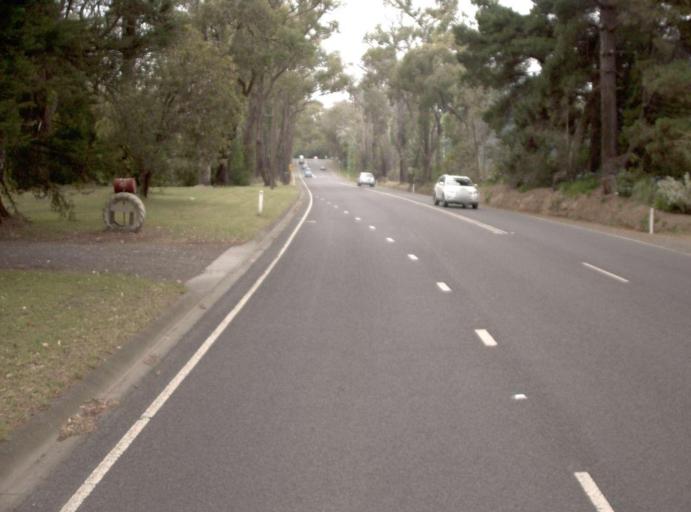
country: AU
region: Victoria
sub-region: Yarra Ranges
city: Mount Evelyn
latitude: -37.7641
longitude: 145.4010
